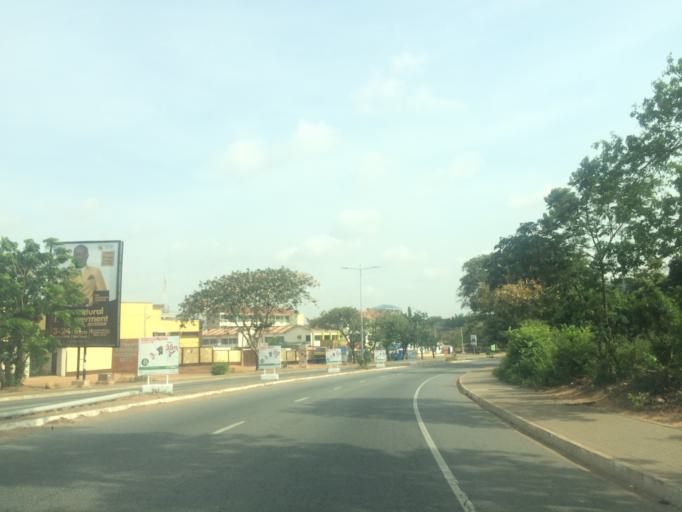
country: GH
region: Greater Accra
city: Accra
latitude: 5.5652
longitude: -0.2021
